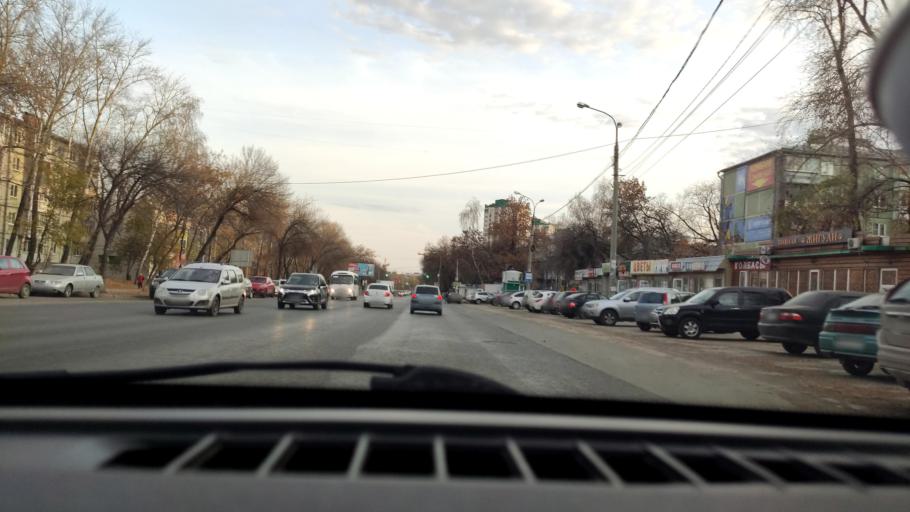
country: RU
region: Samara
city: Samara
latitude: 53.2174
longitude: 50.2080
